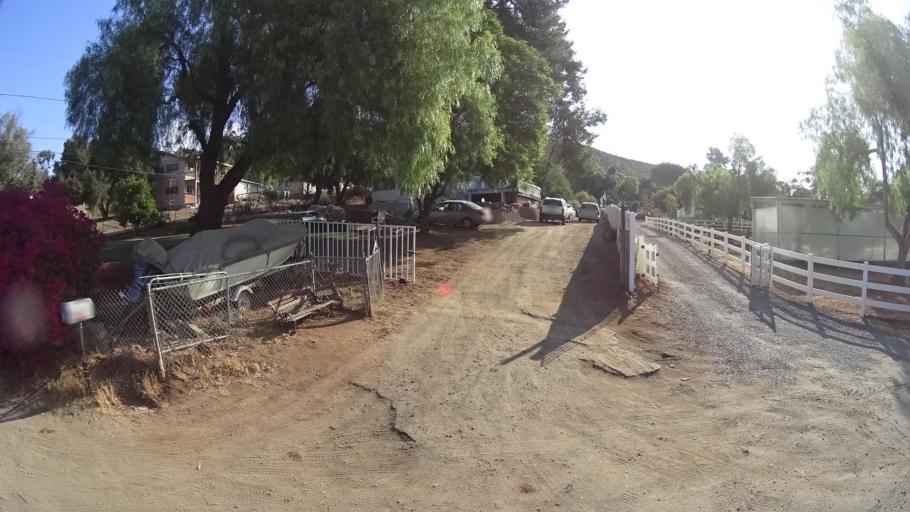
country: US
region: California
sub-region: San Diego County
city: Eucalyptus Hills
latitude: 32.8823
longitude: -116.9542
